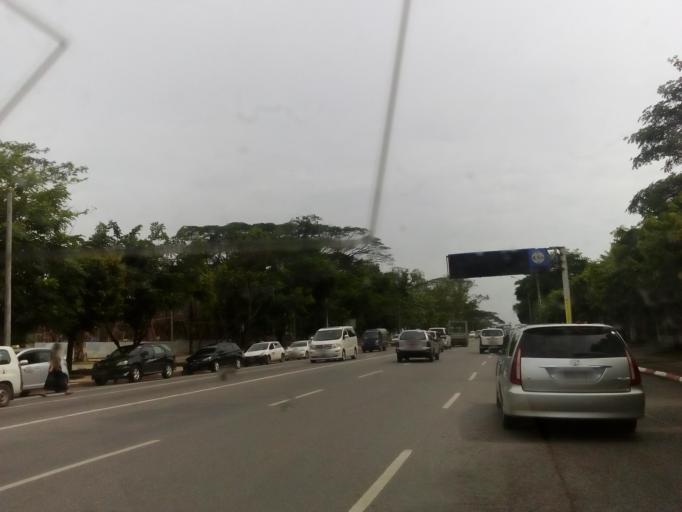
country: MM
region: Yangon
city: Yangon
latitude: 16.8293
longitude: 96.1547
